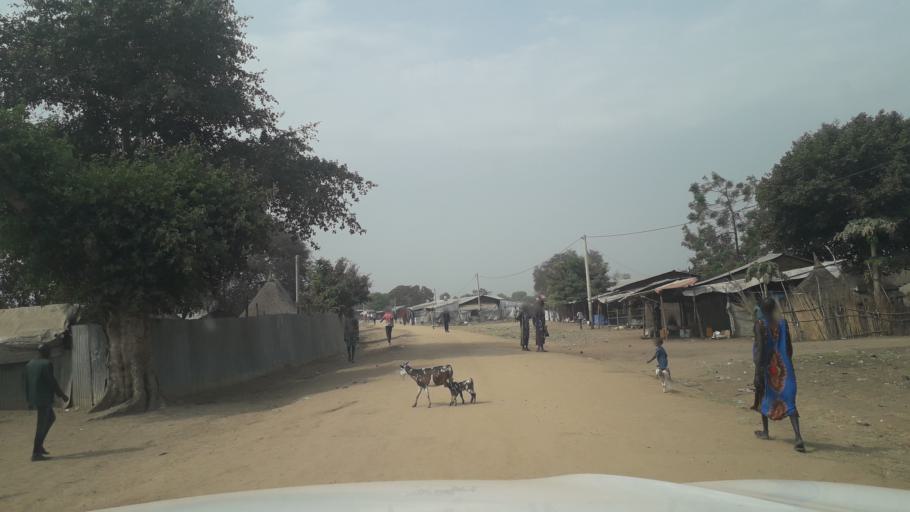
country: ET
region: Gambela
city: Gambela
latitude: 8.3042
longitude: 33.6851
